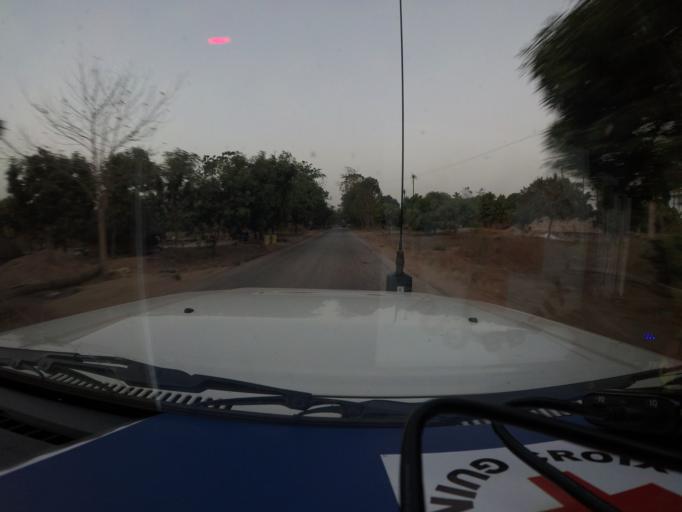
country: GN
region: Kindia
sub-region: Kindia
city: Kindia
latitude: 9.9267
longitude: -12.9910
